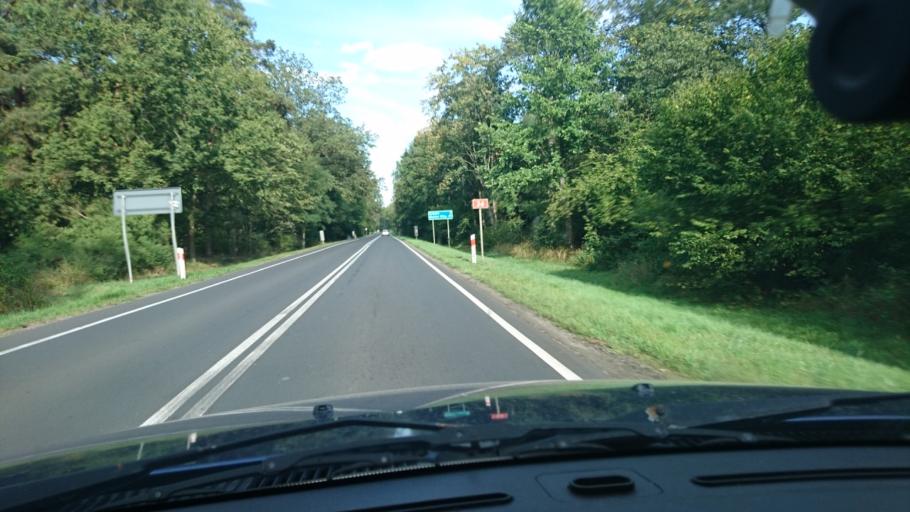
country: PL
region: Greater Poland Voivodeship
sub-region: Powiat krotoszynski
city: Kobylin
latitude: 51.7082
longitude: 17.1896
